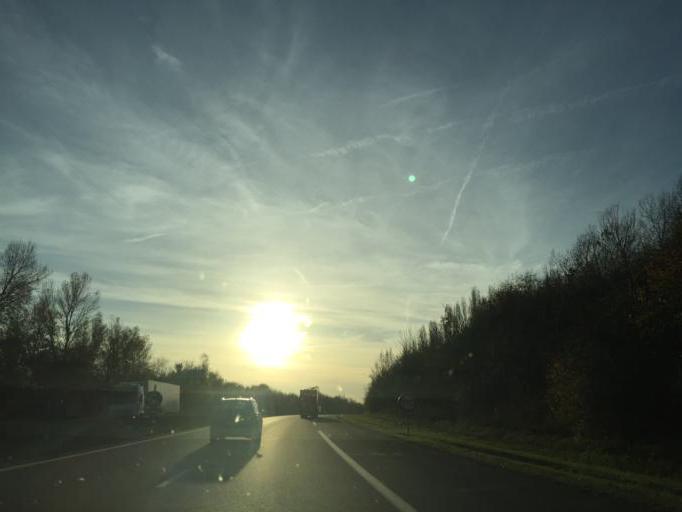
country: FR
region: Rhone-Alpes
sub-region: Departement du Rhone
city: Simandres
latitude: 45.6157
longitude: 4.8871
